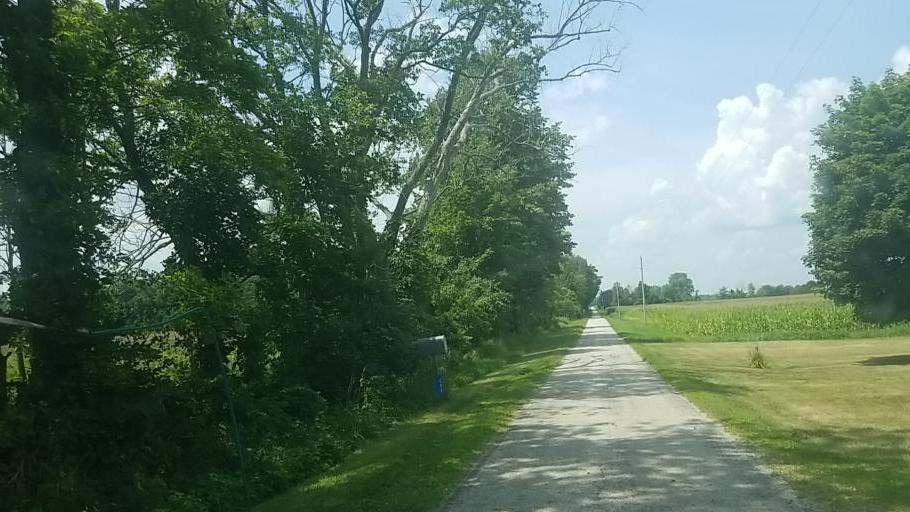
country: US
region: Ohio
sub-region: Crawford County
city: Bucyrus
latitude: 40.7462
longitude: -83.0979
